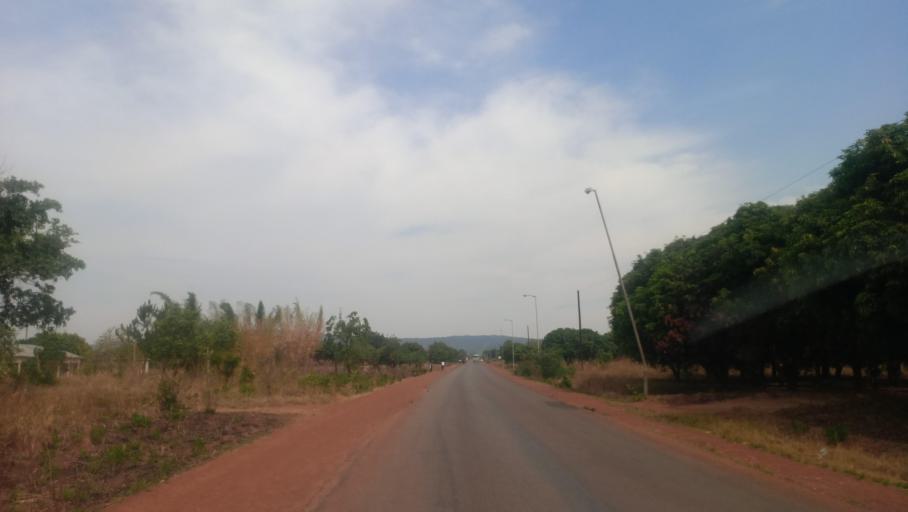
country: ZM
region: Northern
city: Mpika
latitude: -11.8344
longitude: 31.4259
